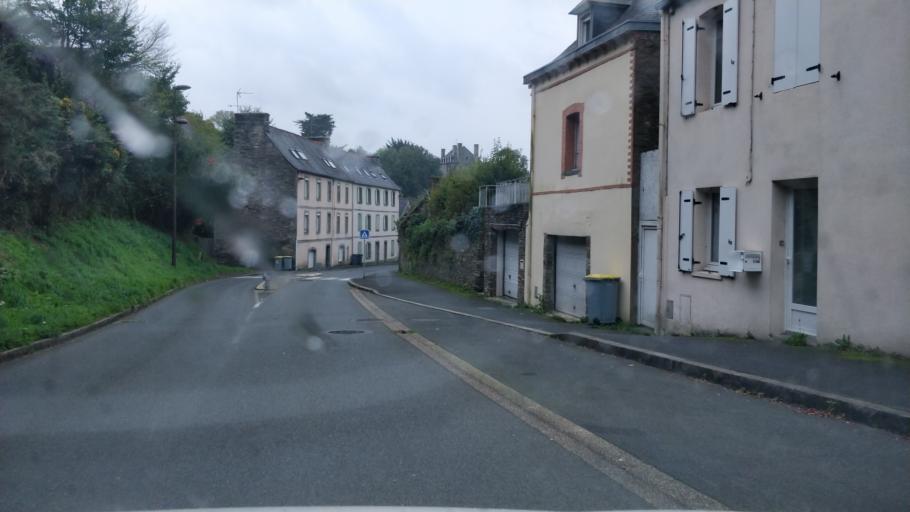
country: FR
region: Brittany
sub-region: Departement des Cotes-d'Armor
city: Lannion
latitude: 48.7365
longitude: -3.4552
